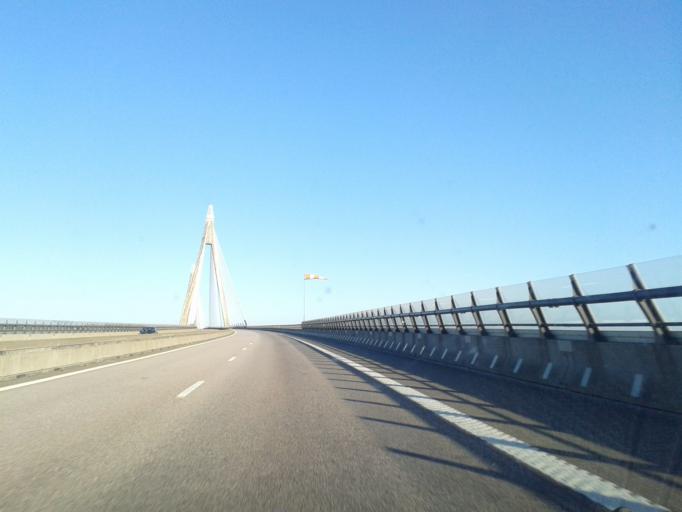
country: SE
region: Vaestra Goetaland
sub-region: Uddevalla Kommun
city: Uddevalla
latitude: 58.3299
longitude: 11.8354
